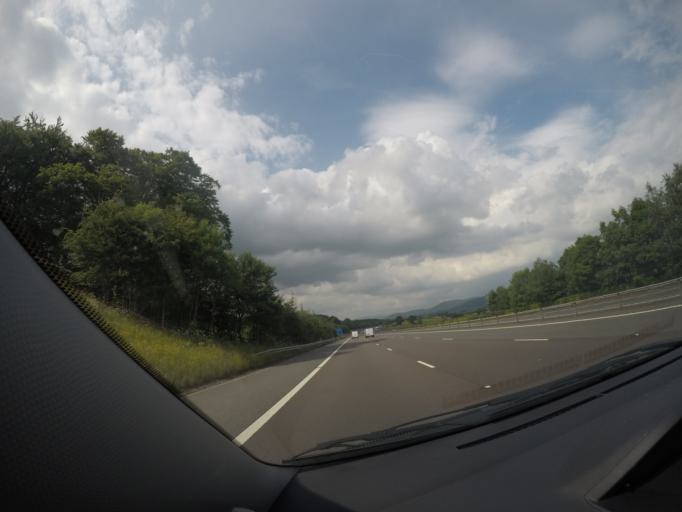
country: GB
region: Scotland
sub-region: Dumfries and Galloway
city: Lochmaben
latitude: 55.2253
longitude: -3.4133
